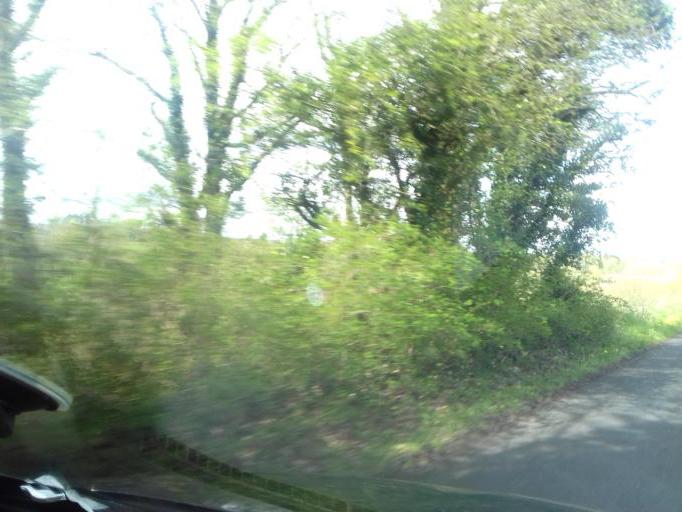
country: GB
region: Northern Ireland
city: Lisnaskea
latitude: 54.1861
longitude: -7.5045
